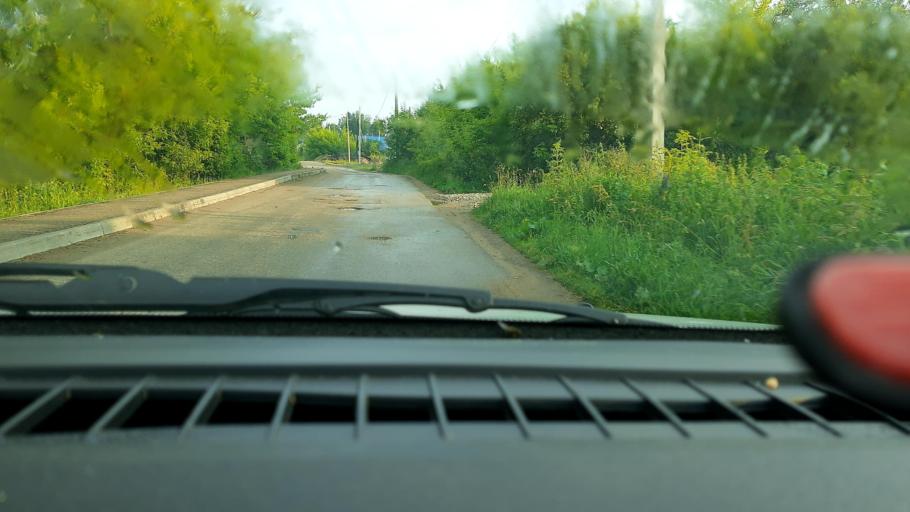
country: RU
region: Nizjnij Novgorod
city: Lukoyanov
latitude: 55.0428
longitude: 44.4941
